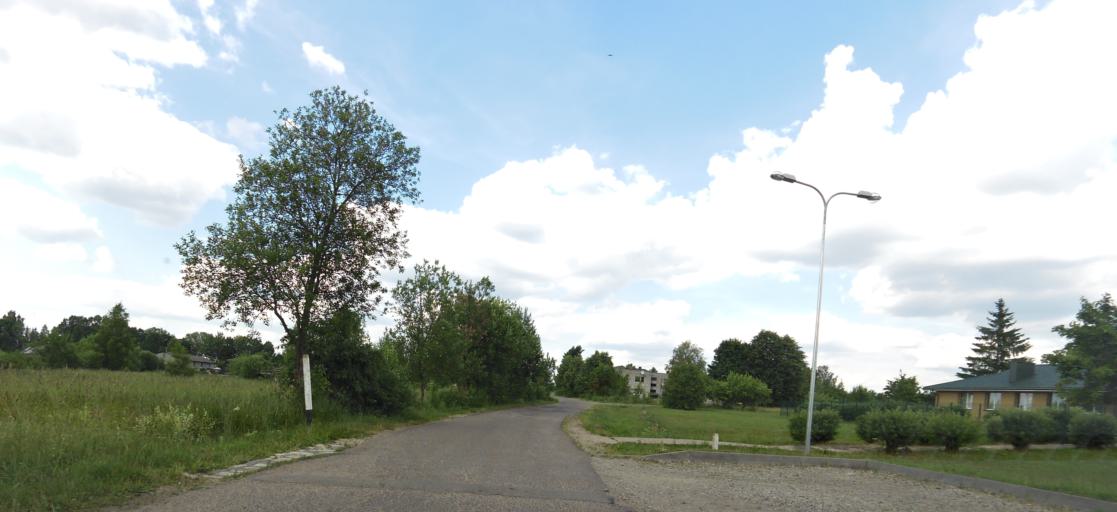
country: LT
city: Skaidiskes
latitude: 54.5348
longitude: 25.6499
